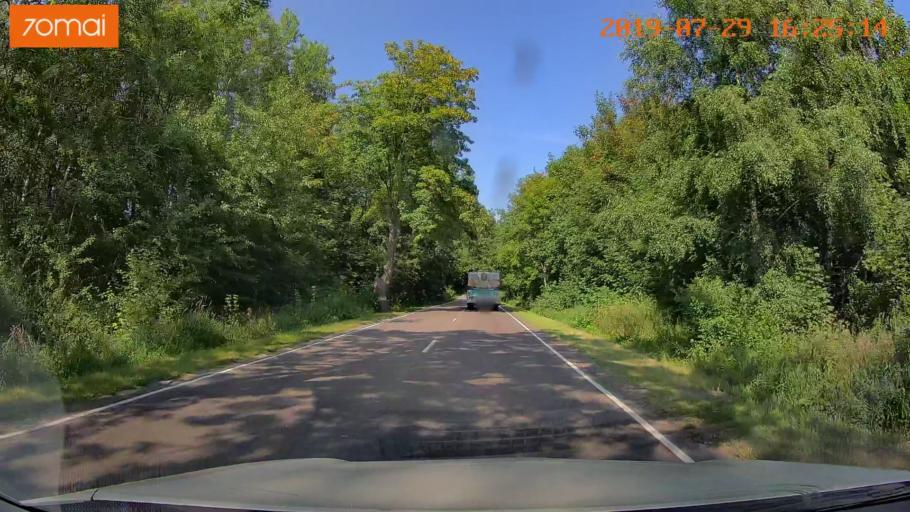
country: RU
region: Kaliningrad
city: Primorsk
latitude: 54.7214
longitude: 19.9646
